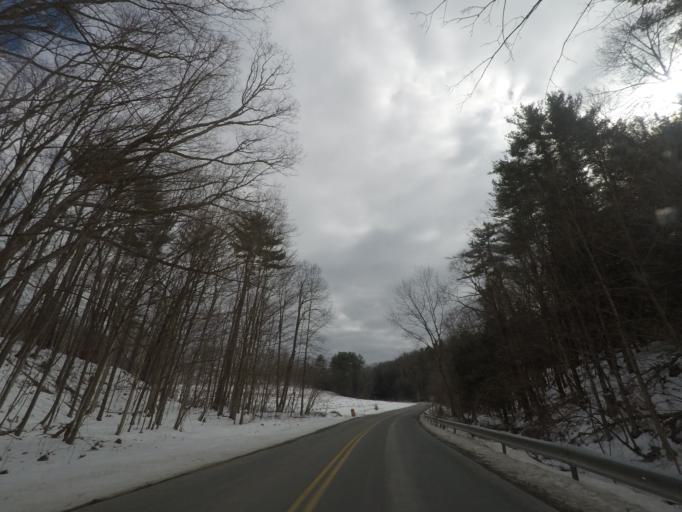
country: US
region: New York
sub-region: Rensselaer County
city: Hoosick Falls
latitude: 42.8831
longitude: -73.4173
